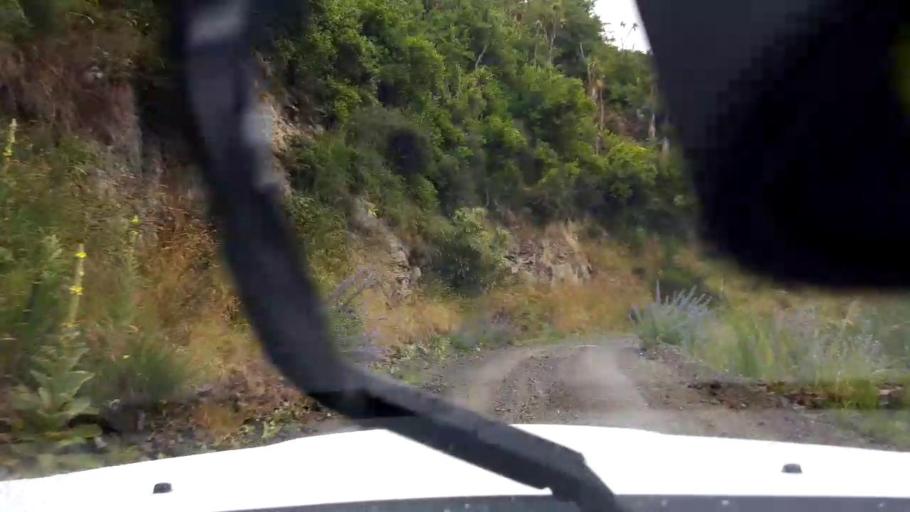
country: NZ
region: Canterbury
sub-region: Timaru District
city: Pleasant Point
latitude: -44.0339
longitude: 170.9984
